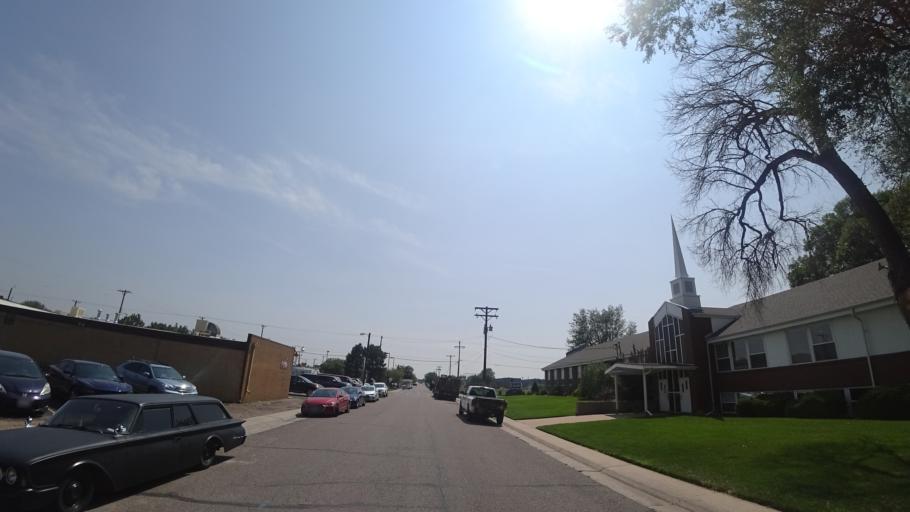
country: US
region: Colorado
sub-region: Arapahoe County
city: Englewood
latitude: 39.6284
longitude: -104.9891
